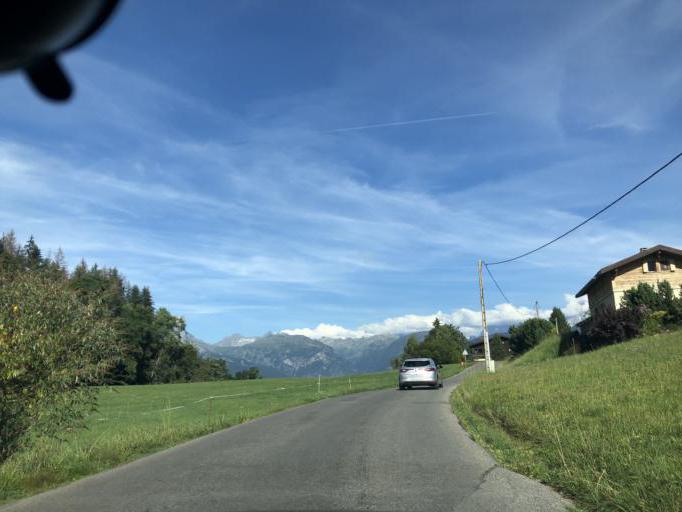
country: FR
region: Rhone-Alpes
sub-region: Departement de la Haute-Savoie
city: Cordon
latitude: 45.9125
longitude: 6.6225
